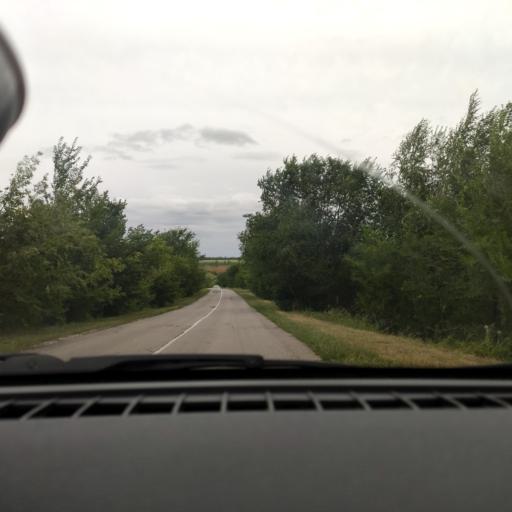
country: RU
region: Samara
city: Georgiyevka
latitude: 53.5134
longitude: 50.9964
